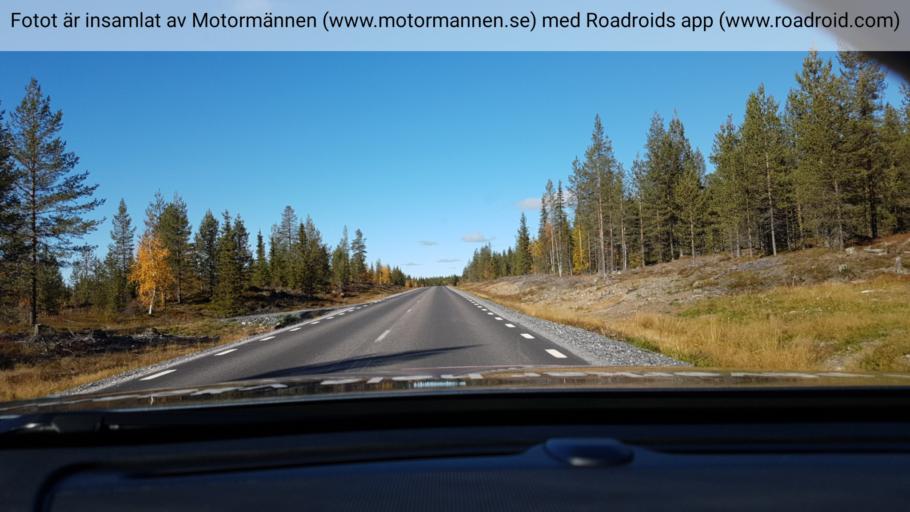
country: SE
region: Norrbotten
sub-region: Gallivare Kommun
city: Gaellivare
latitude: 66.8792
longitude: 20.9483
